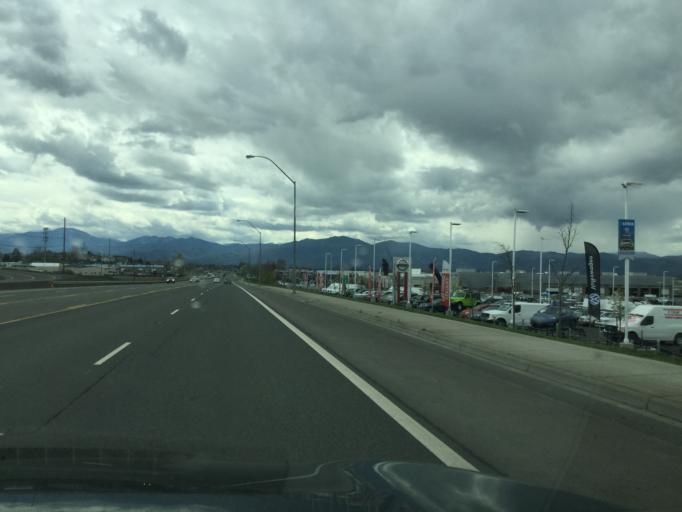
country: US
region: Oregon
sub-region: Jackson County
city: White City
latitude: 42.3812
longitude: -122.8561
